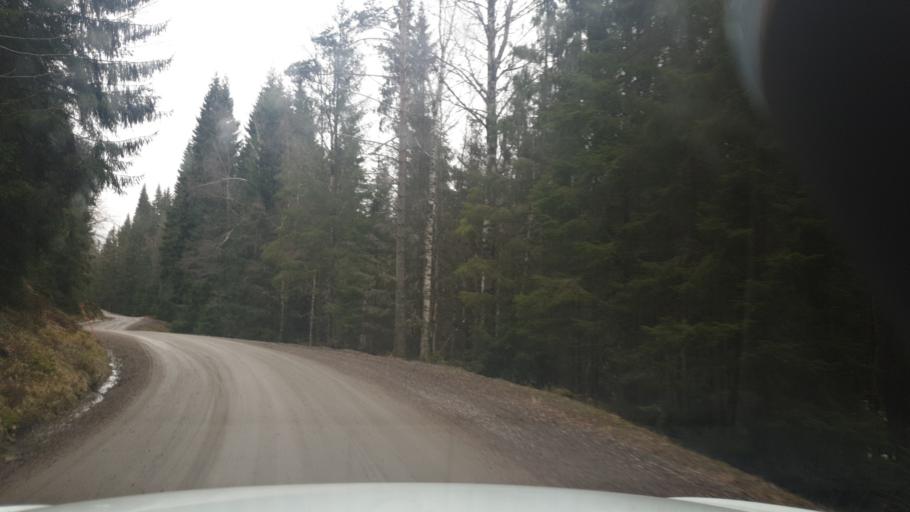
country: NO
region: Ostfold
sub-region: Romskog
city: Romskog
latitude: 59.7131
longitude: 12.0212
